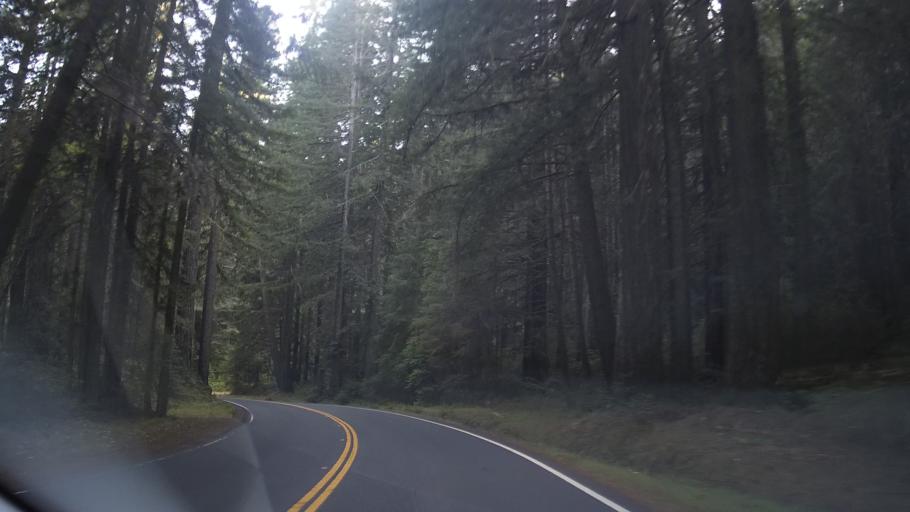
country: US
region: California
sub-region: Mendocino County
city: Brooktrails
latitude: 39.3519
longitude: -123.5617
